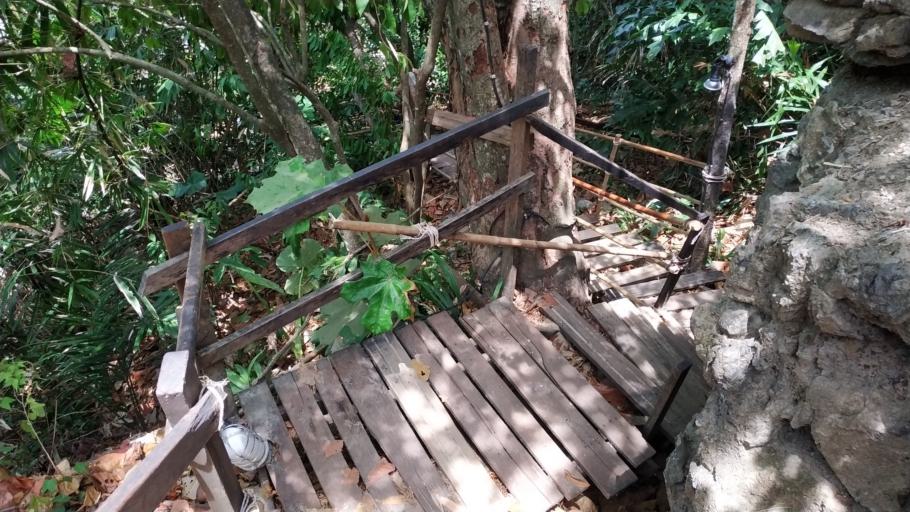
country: TH
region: Phangnga
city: Ban Ao Nang
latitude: 8.0251
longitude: 98.8280
